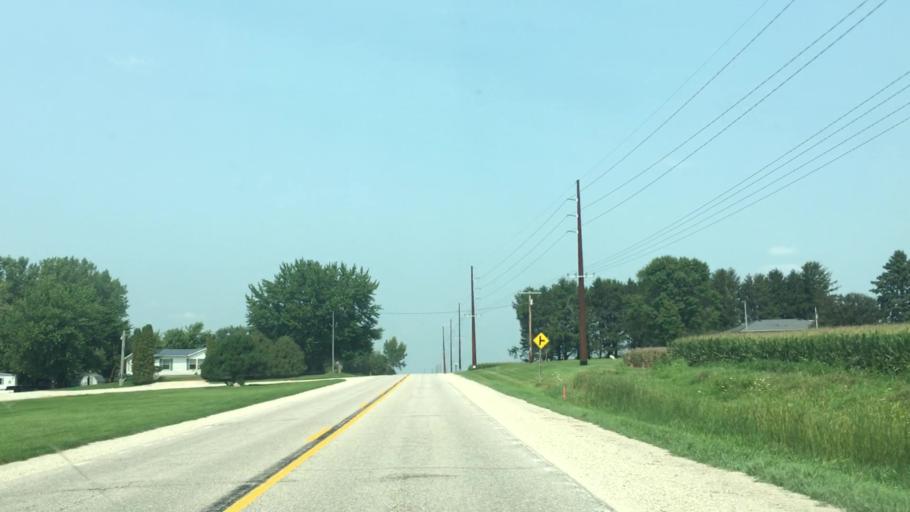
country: US
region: Iowa
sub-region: Buchanan County
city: Independence
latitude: 42.4190
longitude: -91.8898
